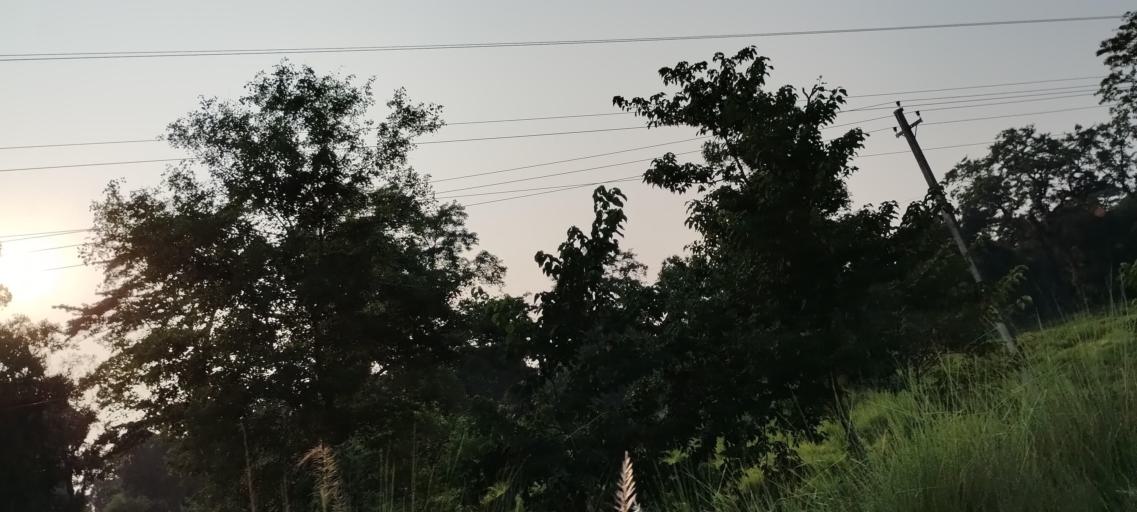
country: NP
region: Far Western
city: Tikapur
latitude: 28.5077
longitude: 81.3247
